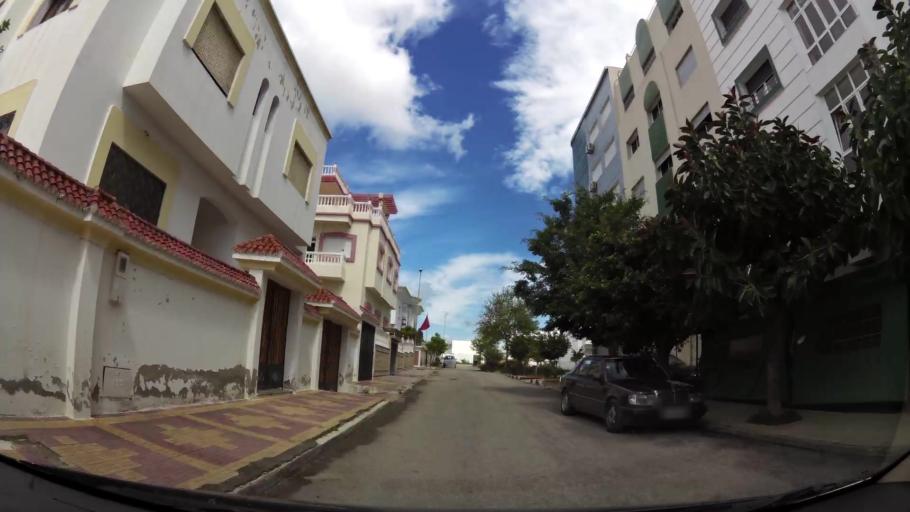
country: MA
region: Tanger-Tetouan
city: Tetouan
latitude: 35.5902
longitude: -5.3417
